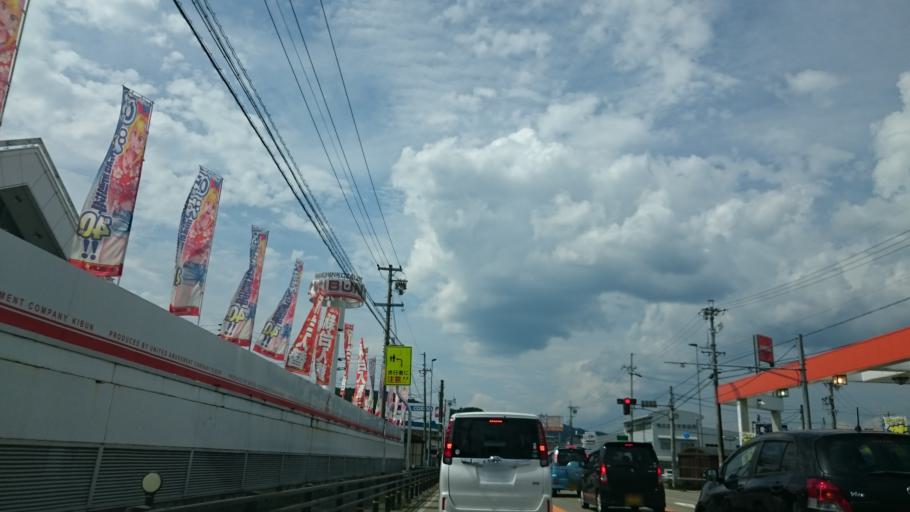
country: JP
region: Gifu
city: Takayama
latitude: 36.1525
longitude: 137.2448
